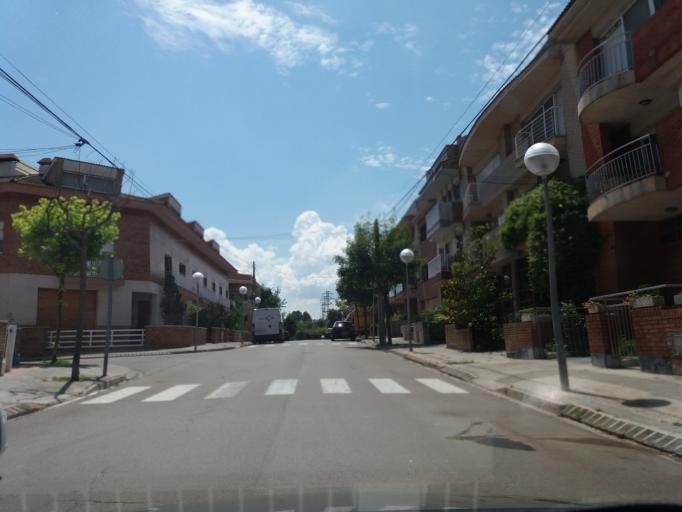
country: ES
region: Catalonia
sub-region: Provincia de Barcelona
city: Sant Joan de Vilatorrada
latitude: 41.7379
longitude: 1.7993
